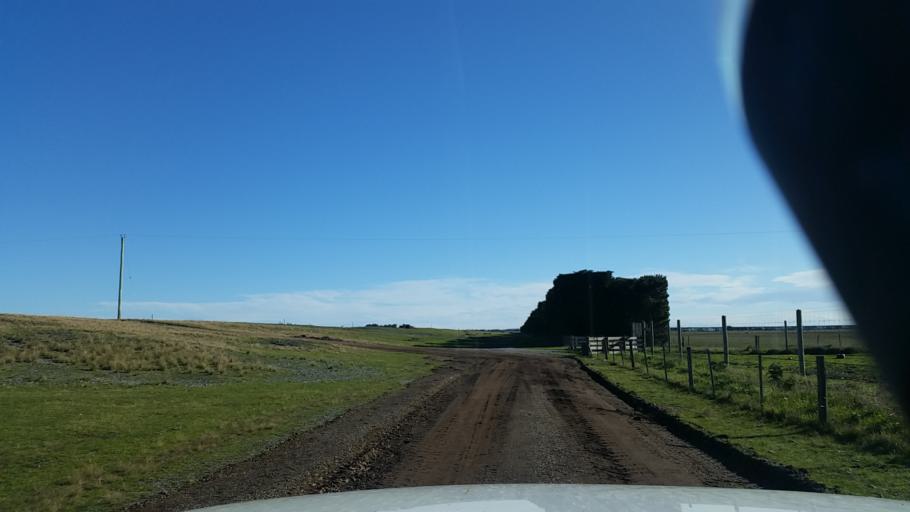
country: NZ
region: Canterbury
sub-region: Selwyn District
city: Lincoln
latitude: -43.8135
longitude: 172.6374
